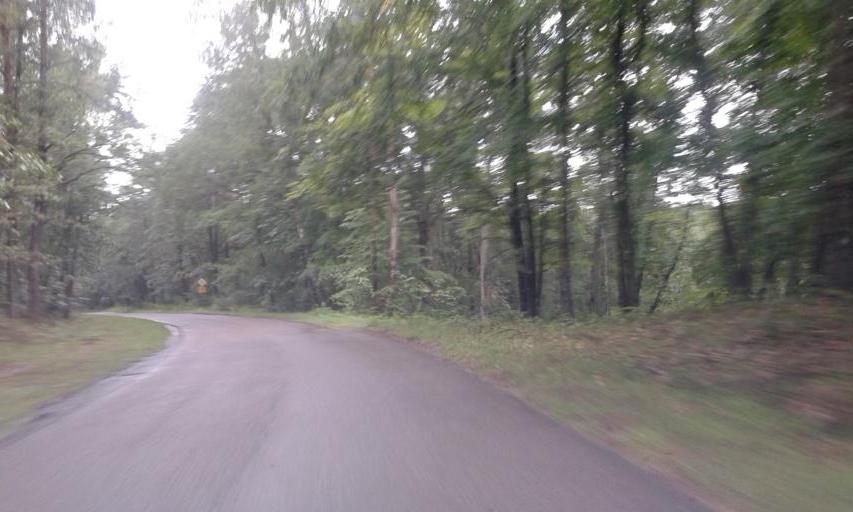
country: PL
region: West Pomeranian Voivodeship
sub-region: Powiat szczecinecki
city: Borne Sulinowo
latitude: 53.5273
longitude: 16.4942
